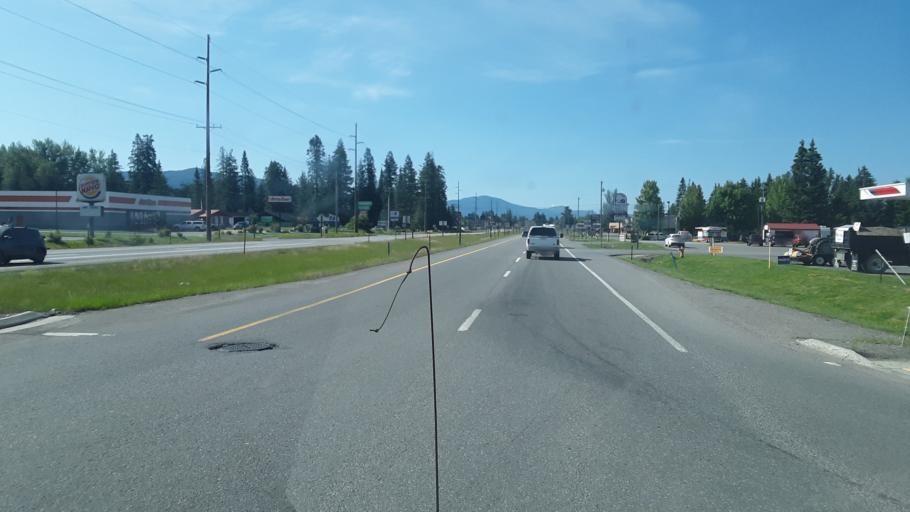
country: US
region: Idaho
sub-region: Bonner County
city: Ponderay
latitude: 48.3091
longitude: -116.5464
